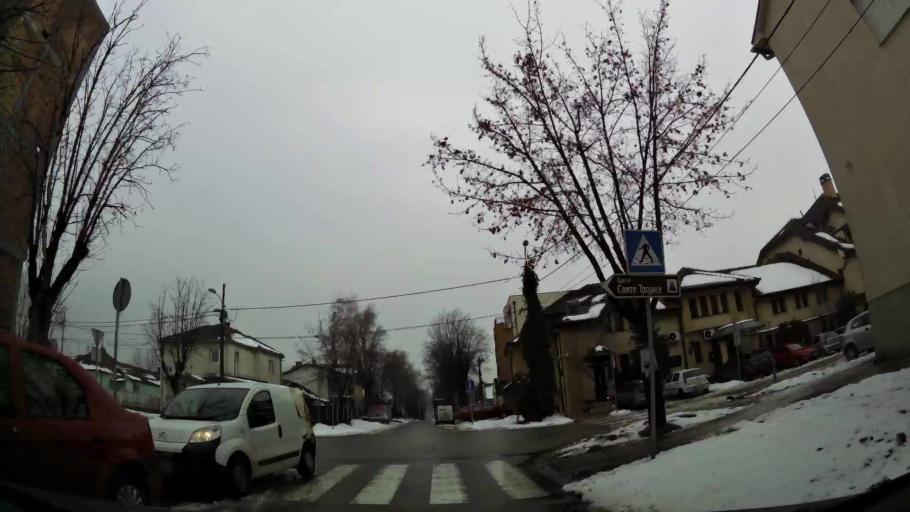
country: RS
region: Central Serbia
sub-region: Belgrade
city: Zemun
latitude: 44.8503
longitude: 20.3946
